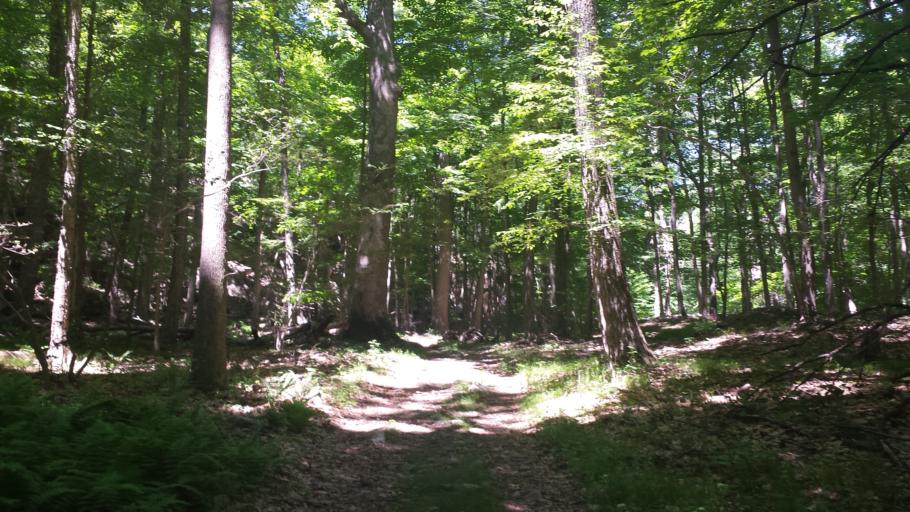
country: US
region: New York
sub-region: Westchester County
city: Pound Ridge
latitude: 41.2448
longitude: -73.5787
